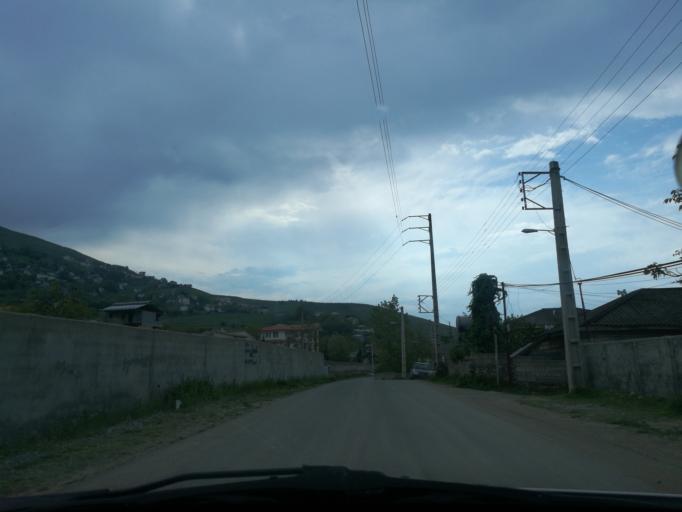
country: IR
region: Mazandaran
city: `Abbasabad
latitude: 36.5329
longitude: 51.2249
